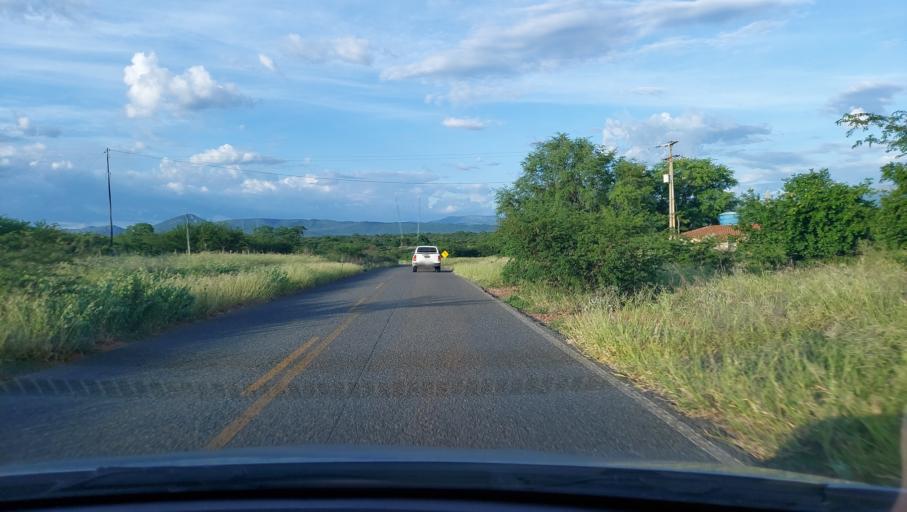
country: BR
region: Bahia
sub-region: Oliveira Dos Brejinhos
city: Beira Rio
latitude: -12.1977
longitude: -42.5379
